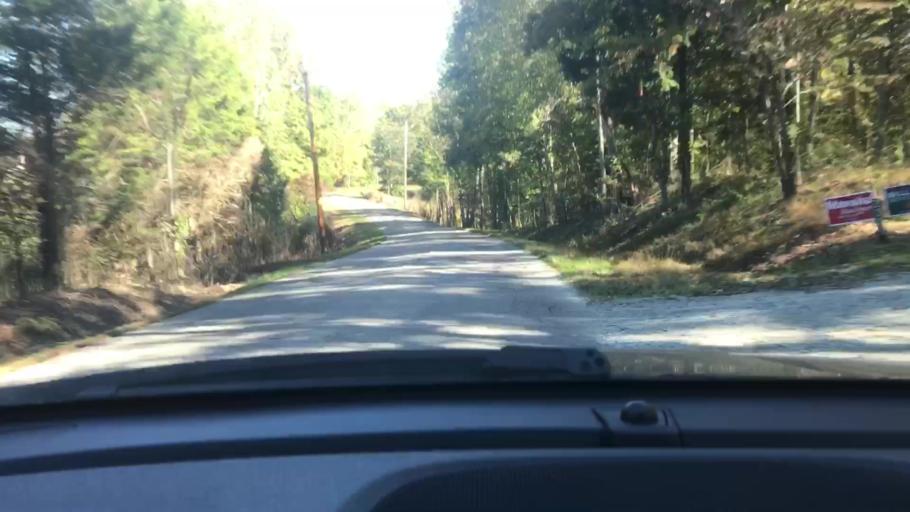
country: US
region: Tennessee
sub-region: Dickson County
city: Charlotte
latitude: 36.1800
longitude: -87.2928
